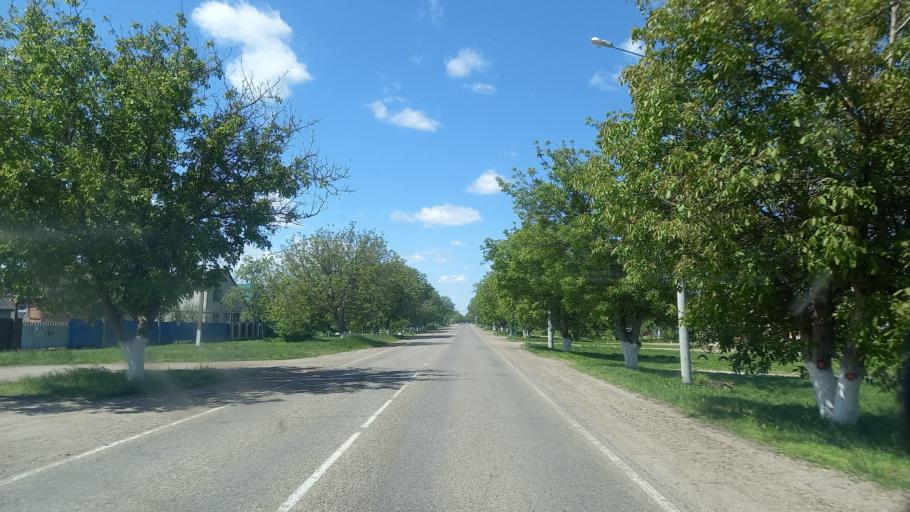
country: RU
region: Krasnodarskiy
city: Novoukrainskoye
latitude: 45.3802
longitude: 40.4965
